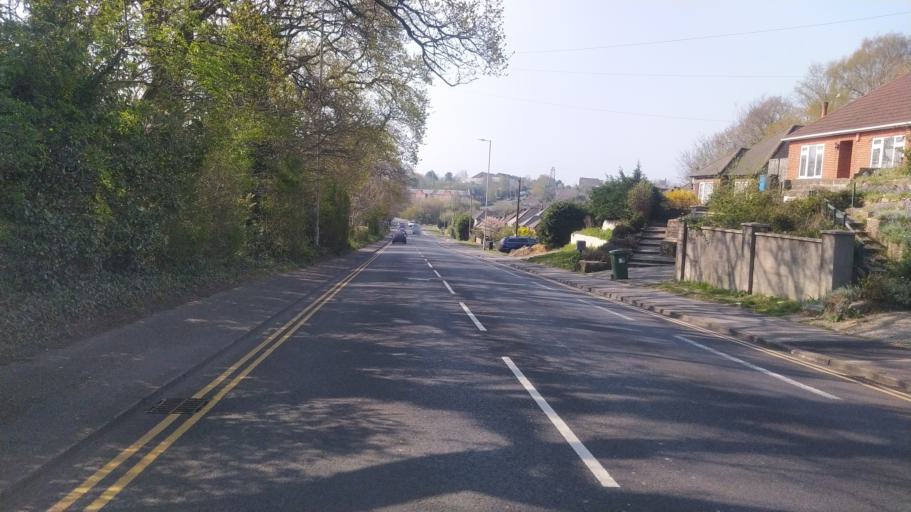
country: GB
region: England
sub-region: Dorset
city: Parkstone
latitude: 50.7443
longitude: -1.9113
